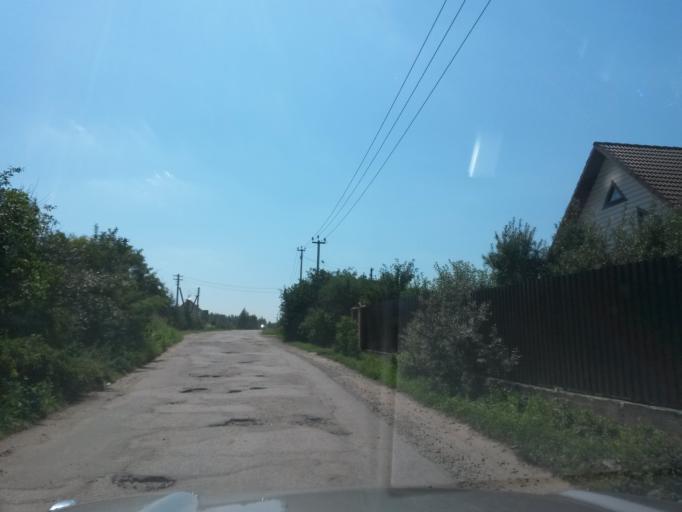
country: RU
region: Moskovskaya
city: Stolbovaya
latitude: 55.2674
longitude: 37.4888
